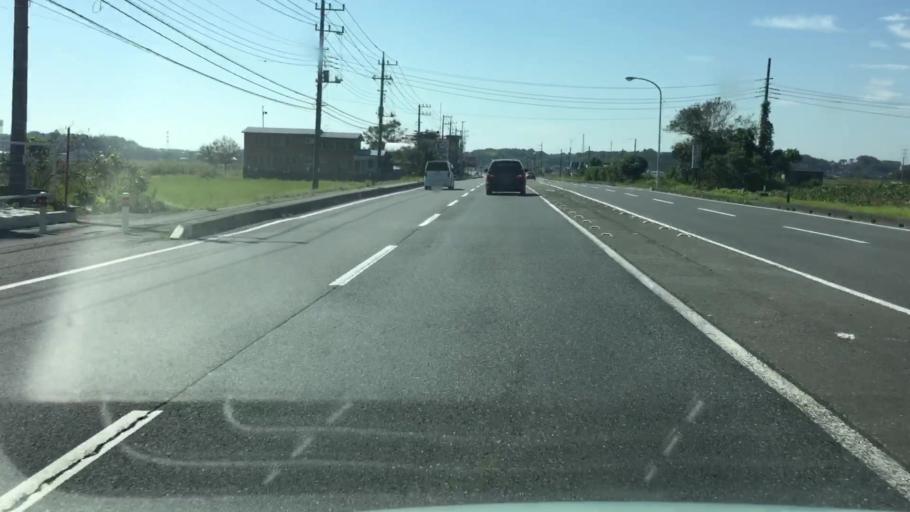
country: JP
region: Ibaraki
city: Ryugasaki
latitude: 35.8938
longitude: 140.1634
